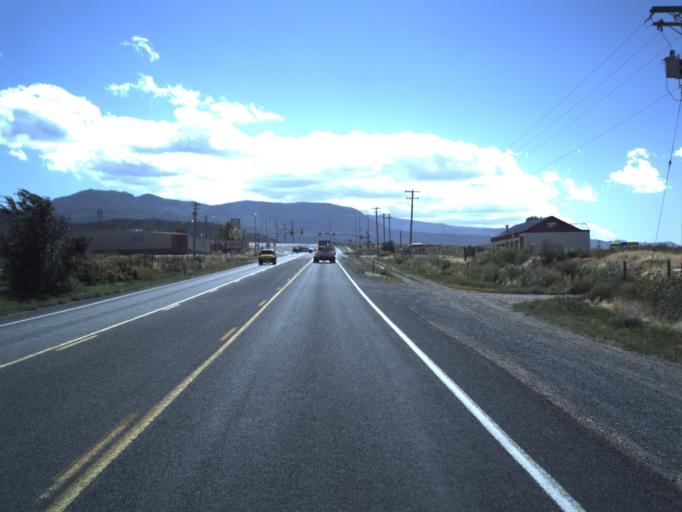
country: US
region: Utah
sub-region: Iron County
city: Enoch
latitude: 37.7339
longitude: -113.0553
